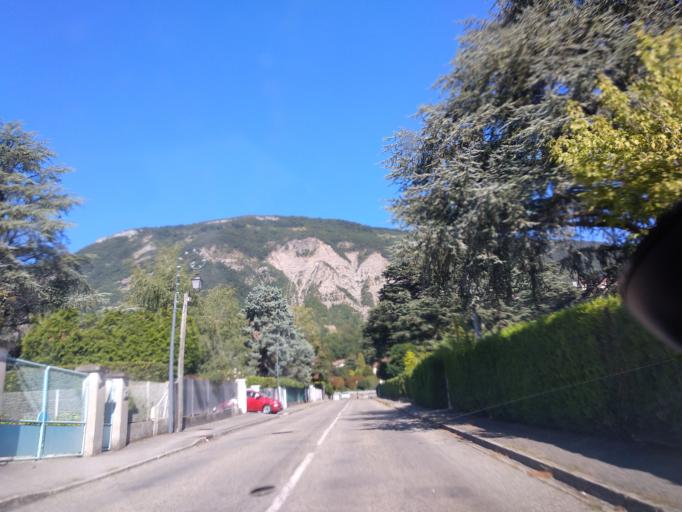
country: FR
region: Rhone-Alpes
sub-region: Departement de l'Isere
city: La Tronche
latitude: 45.2090
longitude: 5.7536
